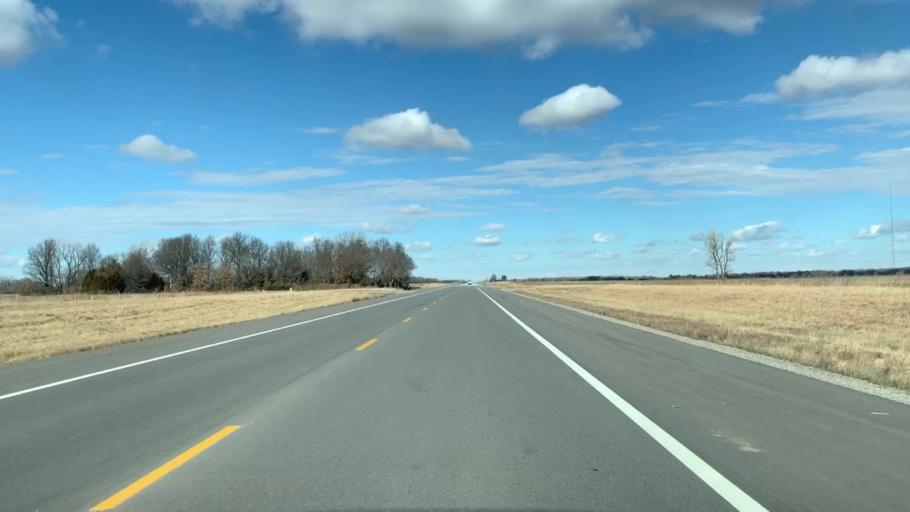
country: US
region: Kansas
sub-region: Cherokee County
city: Columbus
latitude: 37.2877
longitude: -94.8322
